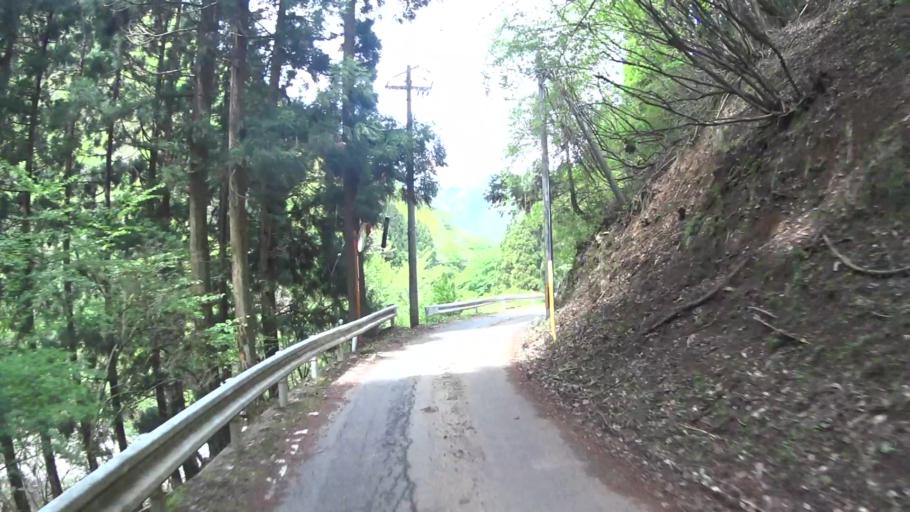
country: JP
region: Kyoto
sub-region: Kyoto-shi
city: Kamigyo-ku
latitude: 35.1687
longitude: 135.7416
